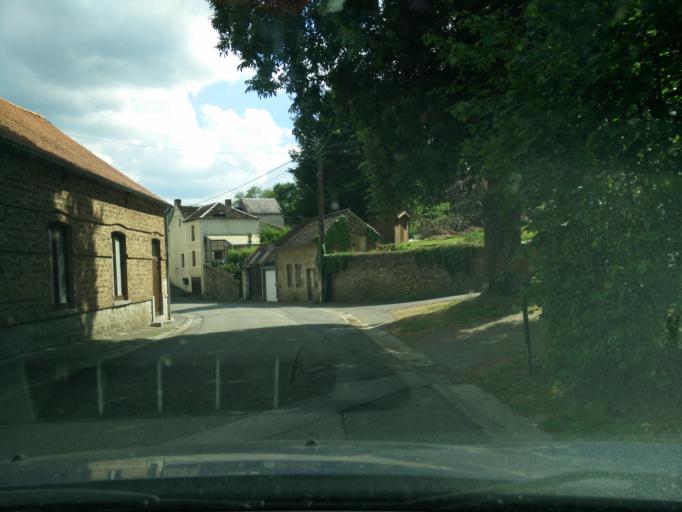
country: FR
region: Champagne-Ardenne
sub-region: Departement des Ardennes
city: Vireux-Molhain
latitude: 50.0818
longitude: 4.6335
